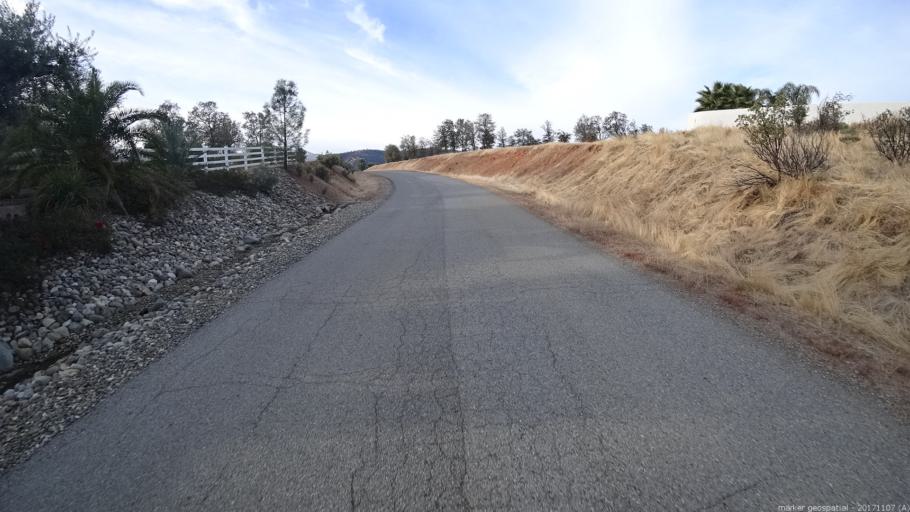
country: US
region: California
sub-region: Shasta County
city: Shasta
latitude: 40.5108
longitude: -122.4748
